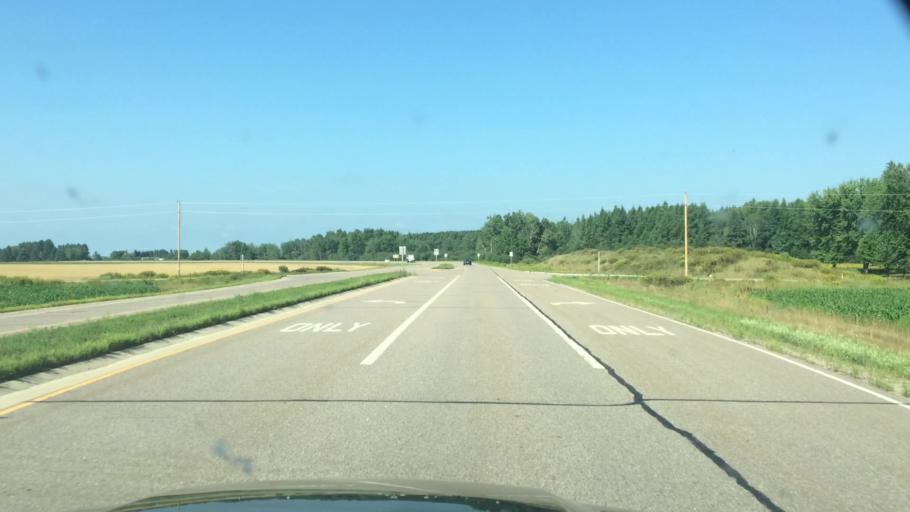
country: US
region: Wisconsin
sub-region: Langlade County
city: Antigo
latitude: 45.1531
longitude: -89.1775
